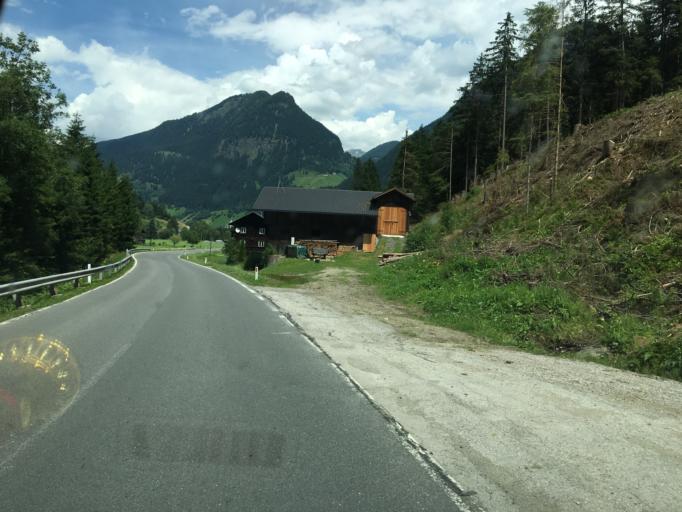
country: AT
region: Carinthia
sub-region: Politischer Bezirk Spittal an der Drau
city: Mortschach
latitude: 46.9011
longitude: 12.9060
